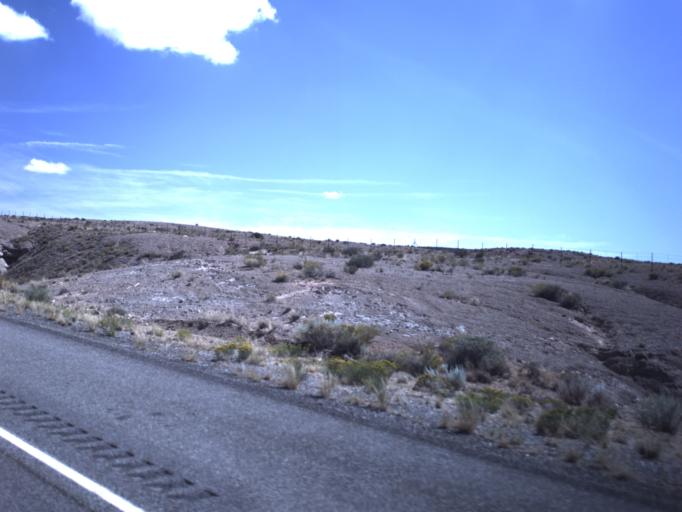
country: US
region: Utah
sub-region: Emery County
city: Ferron
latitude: 38.8440
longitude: -110.9847
